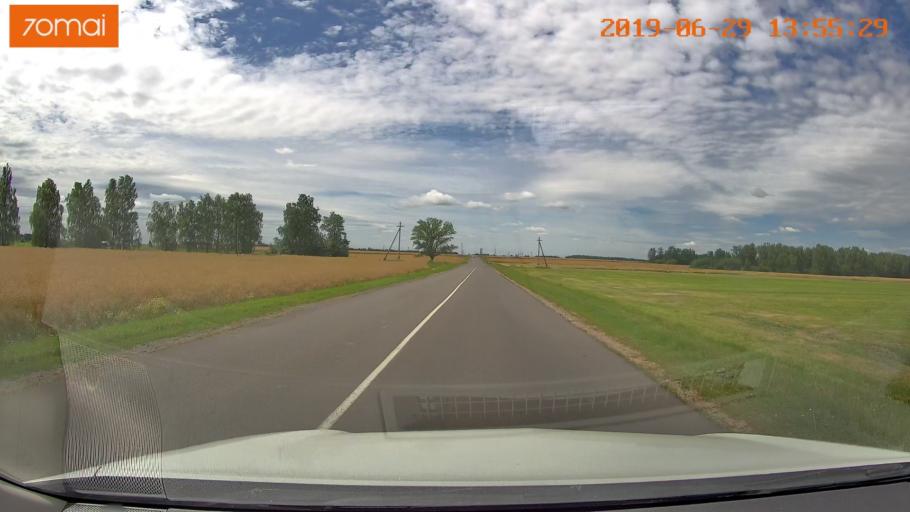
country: BY
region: Minsk
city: Slutsk
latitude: 52.9840
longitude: 27.5192
